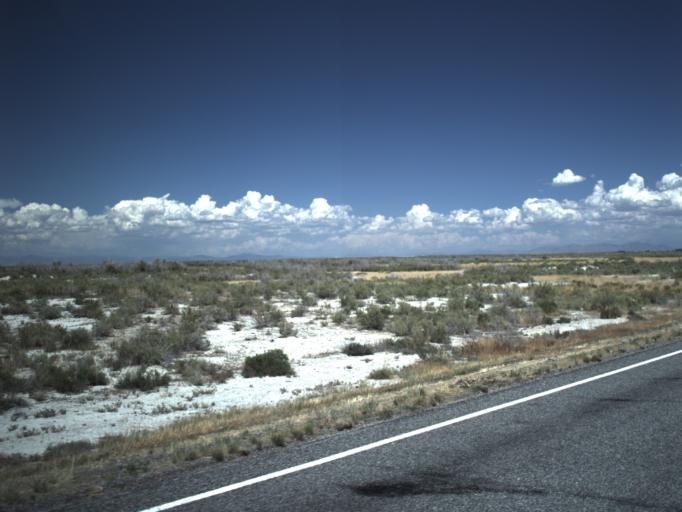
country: US
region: Utah
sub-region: Millard County
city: Delta
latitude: 39.3089
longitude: -112.7826
